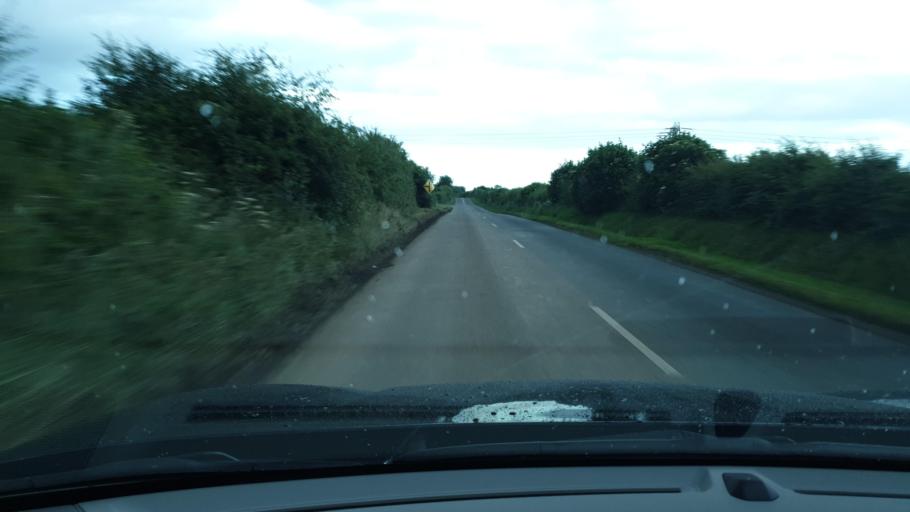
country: IE
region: Leinster
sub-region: An Mhi
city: Navan
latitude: 53.6038
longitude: -6.6155
